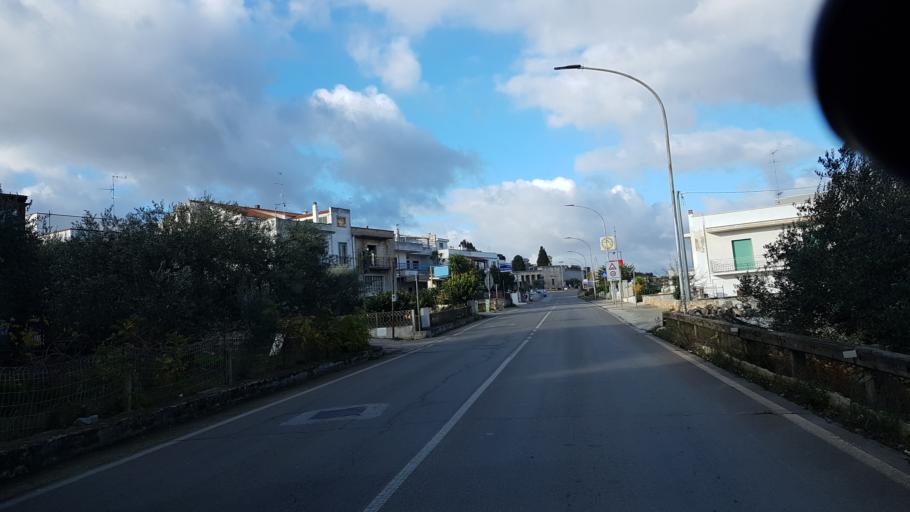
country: IT
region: Apulia
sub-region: Provincia di Bari
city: Alberobello
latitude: 40.7890
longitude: 17.2438
